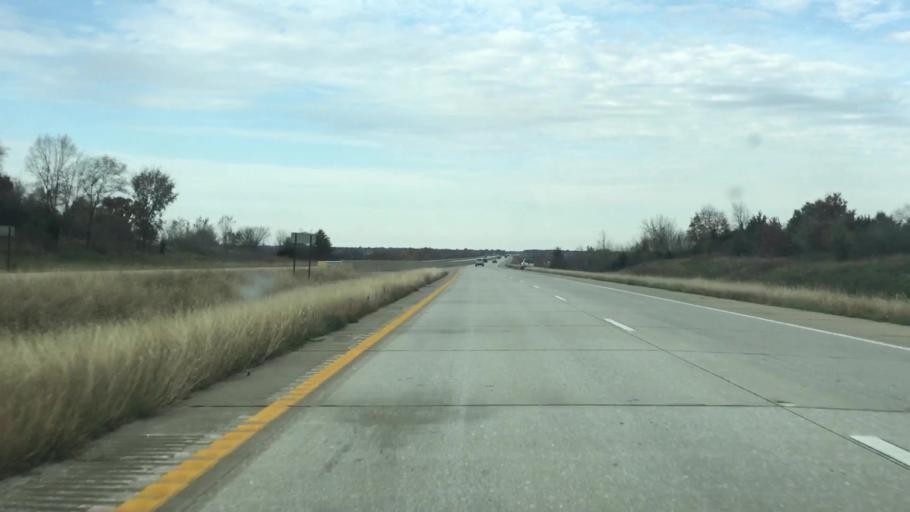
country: US
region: Missouri
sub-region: Henry County
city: Clinton
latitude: 38.3098
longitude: -93.7583
